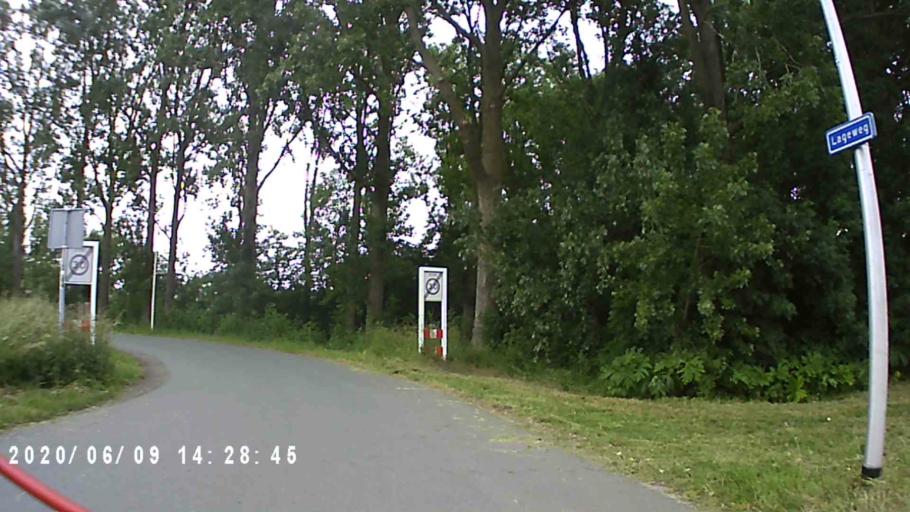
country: NL
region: Groningen
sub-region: Gemeente Bedum
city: Bedum
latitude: 53.3076
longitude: 6.5959
